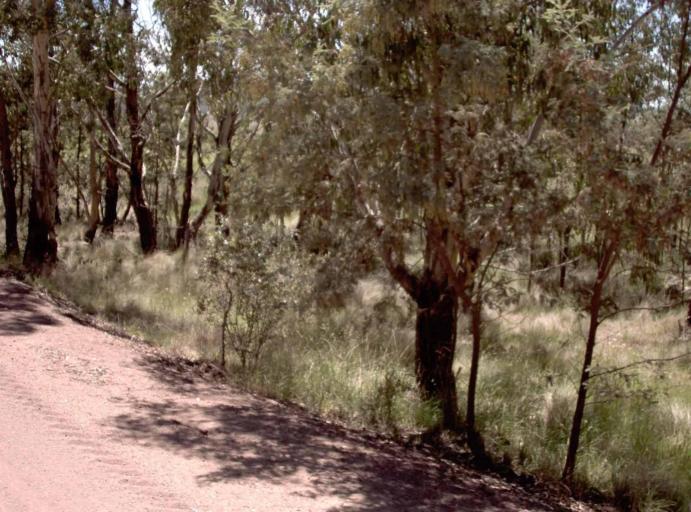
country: AU
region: New South Wales
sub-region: Snowy River
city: Jindabyne
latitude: -37.0249
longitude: 148.2735
